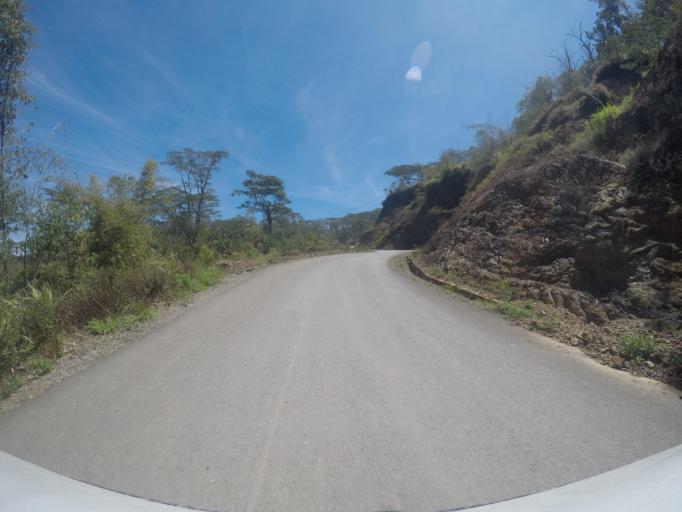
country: TL
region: Ermera
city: Gleno
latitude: -8.7890
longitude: 125.3784
